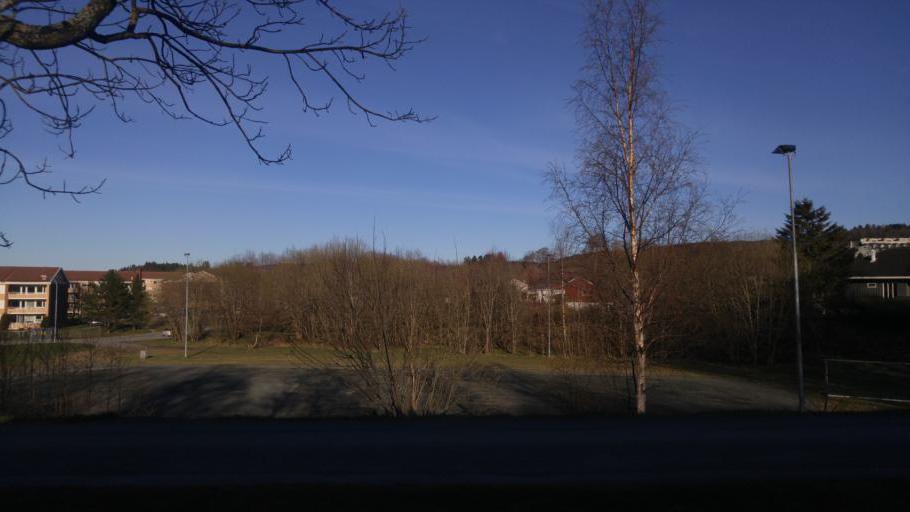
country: NO
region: Sor-Trondelag
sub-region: Trondheim
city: Trondheim
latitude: 63.4150
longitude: 10.4455
